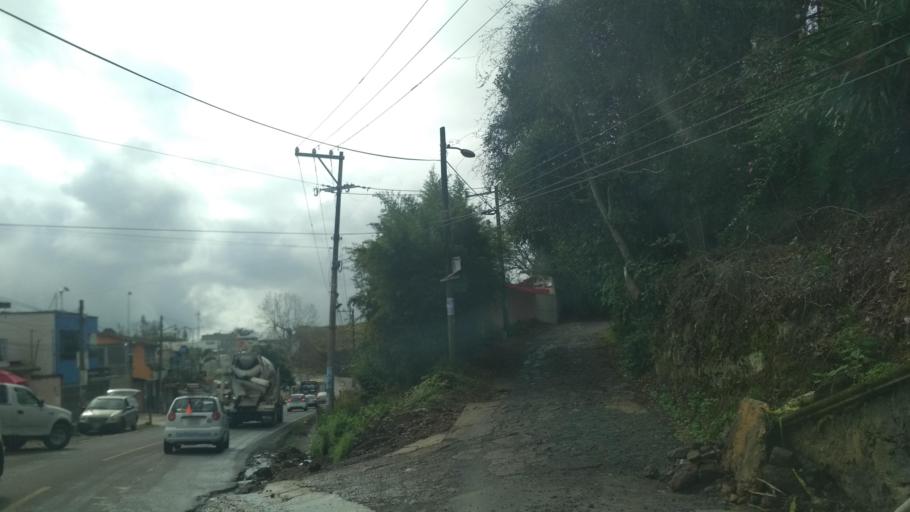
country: MX
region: Veracruz
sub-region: Emiliano Zapata
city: Las Trancas
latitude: 19.5050
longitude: -96.8623
